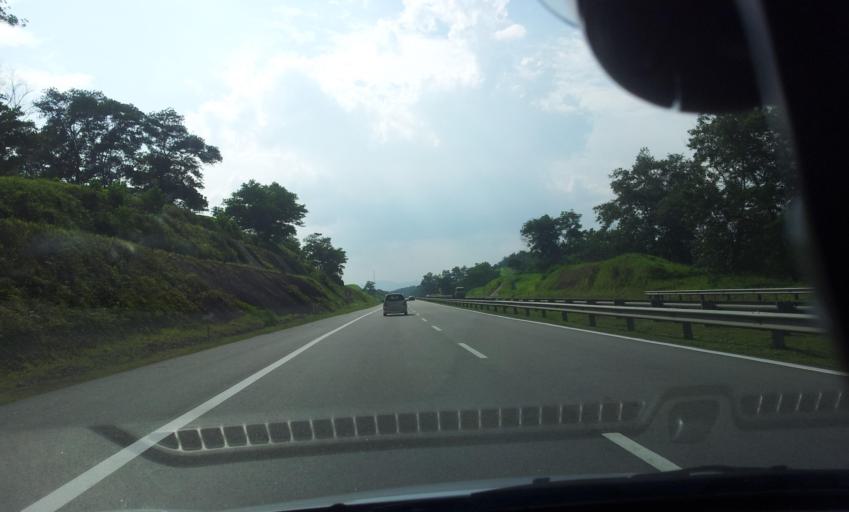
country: MY
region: Pahang
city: Mentekab
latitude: 3.5123
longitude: 102.3340
